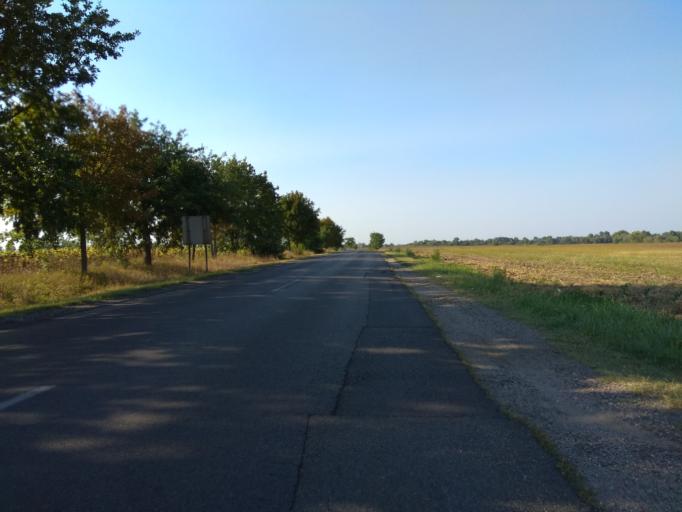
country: HU
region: Borsod-Abauj-Zemplen
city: Onod
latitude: 47.9828
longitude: 20.9269
